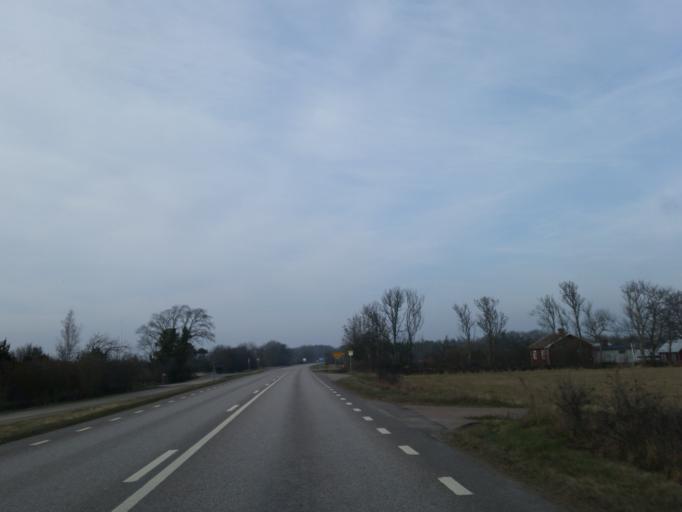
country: SE
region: Kalmar
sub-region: Borgholms Kommun
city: Borgholm
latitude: 56.8931
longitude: 16.7324
